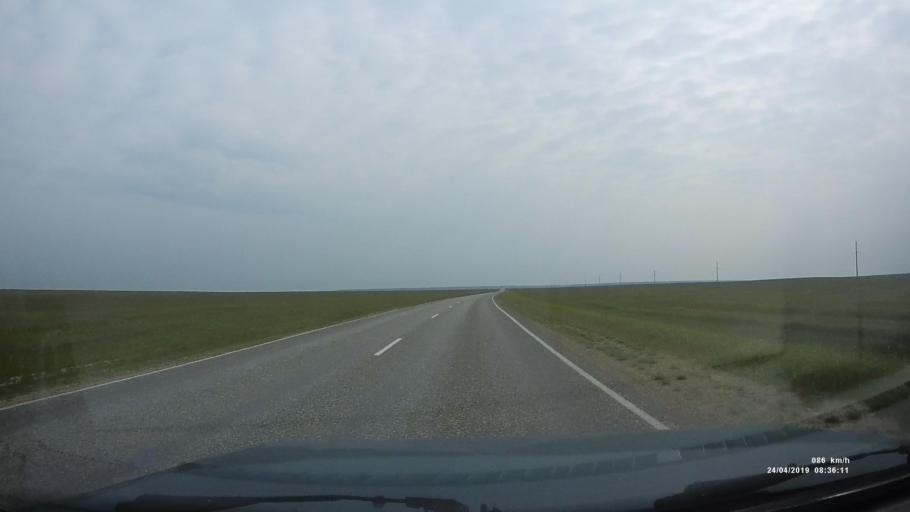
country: RU
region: Kalmykiya
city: Arshan'
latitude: 46.2032
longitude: 43.9302
